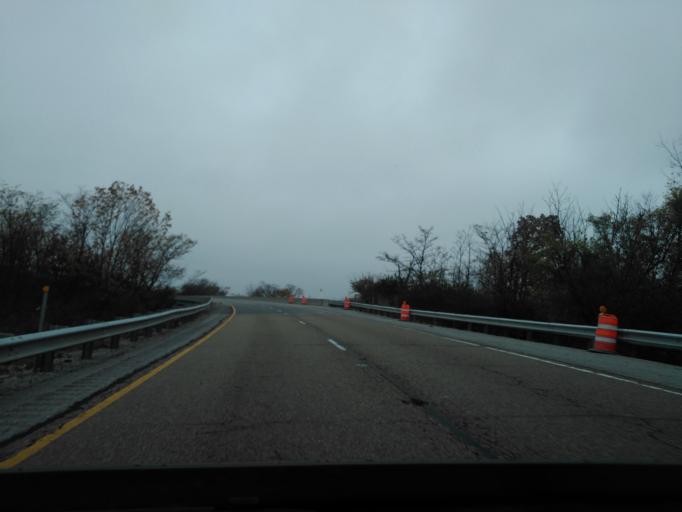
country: US
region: Illinois
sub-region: Madison County
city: Troy
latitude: 38.7496
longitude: -89.9069
